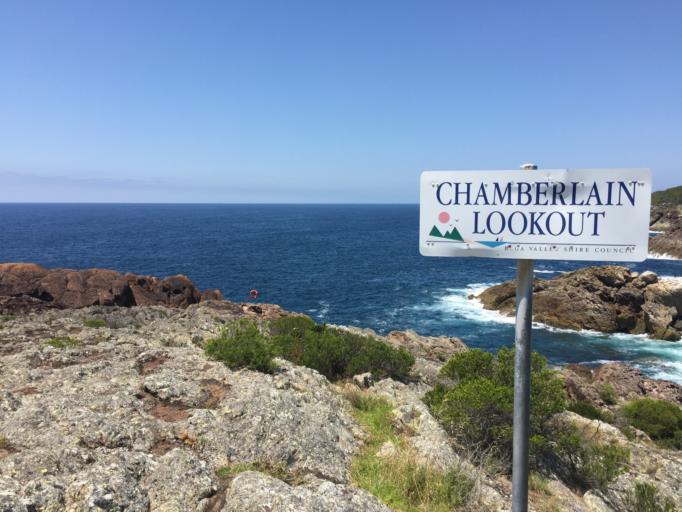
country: AU
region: New South Wales
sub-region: Bega Valley
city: Bega
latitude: -36.7374
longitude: 149.9846
